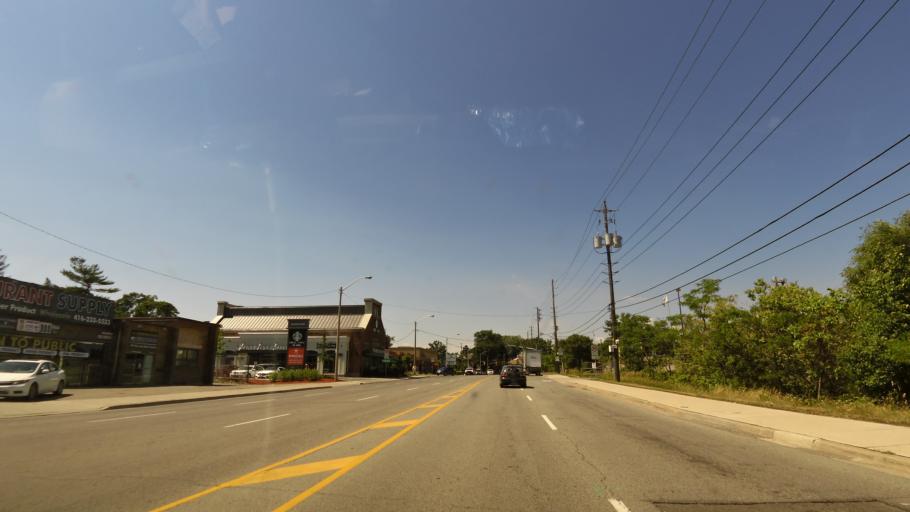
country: CA
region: Ontario
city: Etobicoke
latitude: 43.6277
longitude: -79.4885
